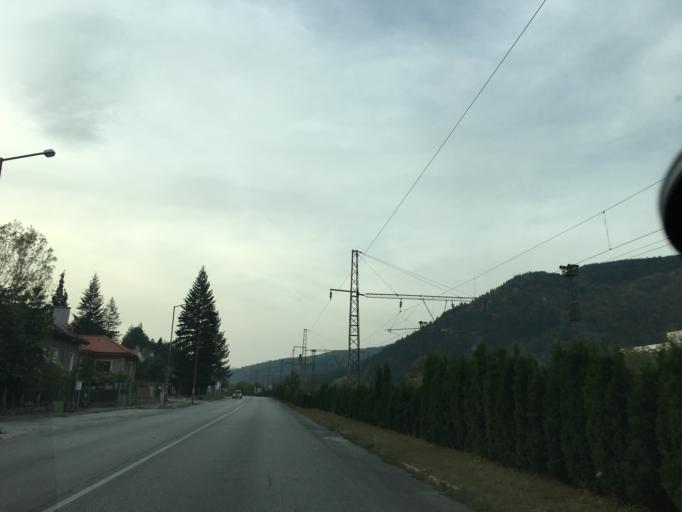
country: BG
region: Pazardzhik
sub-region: Obshtina Belovo
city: Belovo
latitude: 42.2194
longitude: 24.0040
